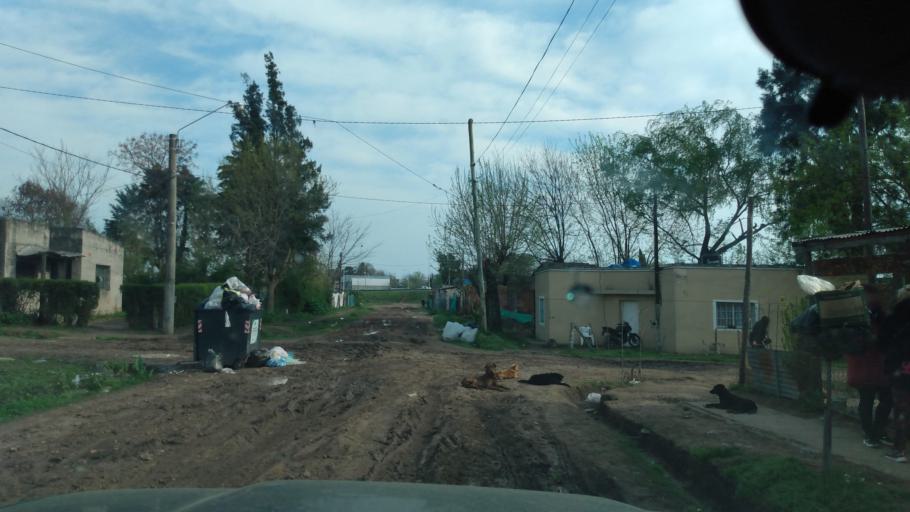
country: AR
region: Buenos Aires
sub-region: Partido de Lujan
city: Lujan
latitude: -34.5488
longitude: -59.1189
